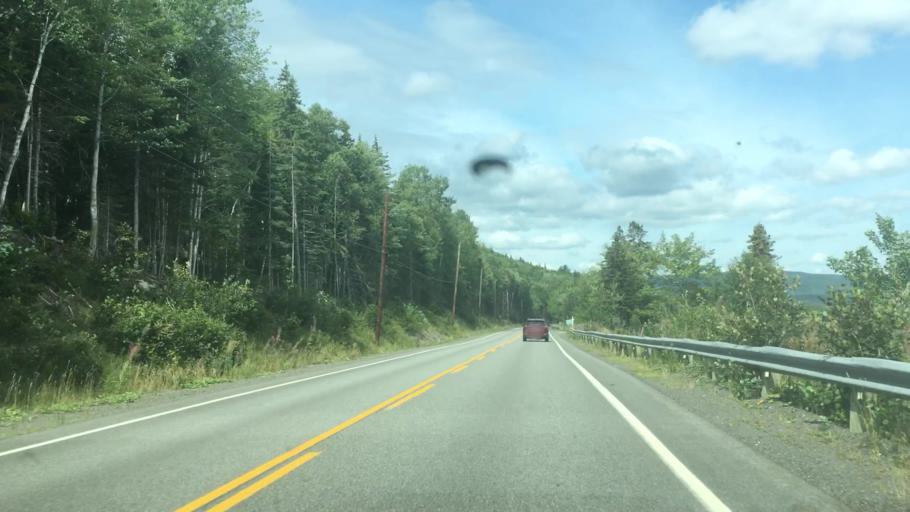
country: CA
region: Nova Scotia
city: Sydney Mines
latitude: 46.2739
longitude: -60.6104
